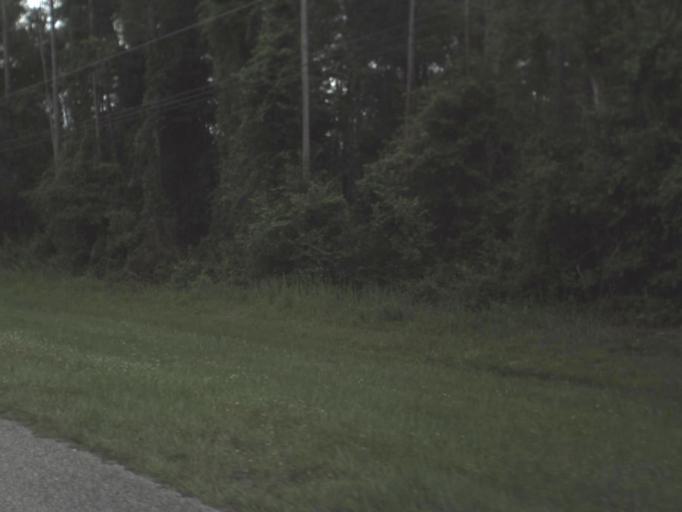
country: US
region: Florida
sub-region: Nassau County
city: Nassau Village-Ratliff
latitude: 30.4586
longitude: -81.7732
